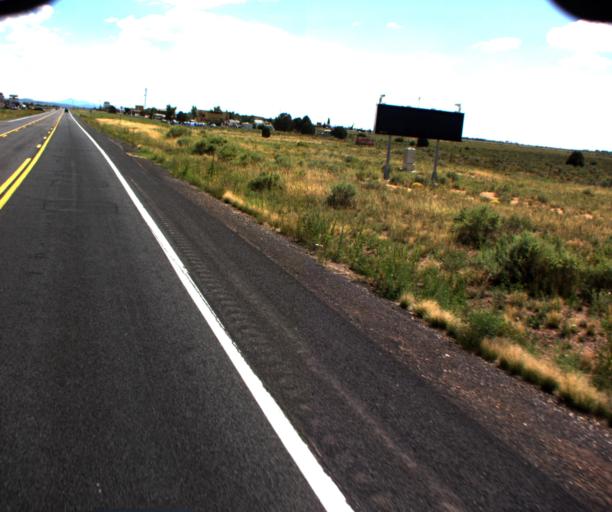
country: US
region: Arizona
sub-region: Coconino County
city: Grand Canyon Village
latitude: 35.6582
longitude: -112.1387
